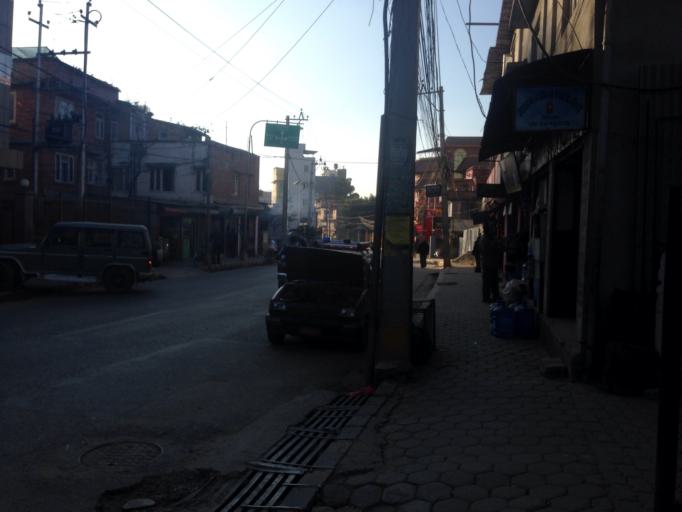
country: NP
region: Central Region
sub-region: Bagmati Zone
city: Kathmandu
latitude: 27.7175
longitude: 85.3288
